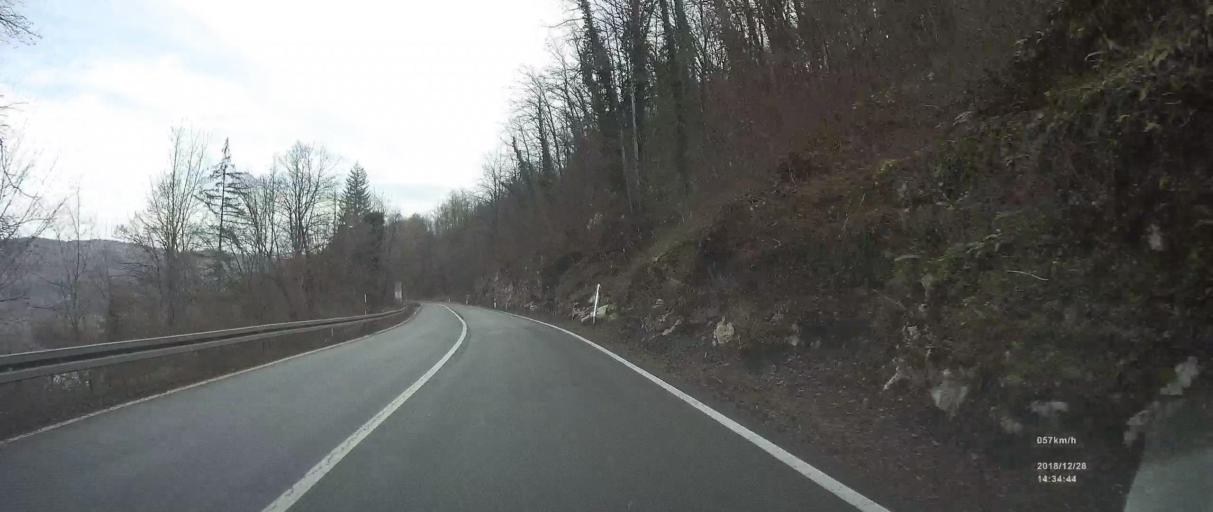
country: HR
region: Primorsko-Goranska
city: Vrbovsko
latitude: 45.4203
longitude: 15.1757
